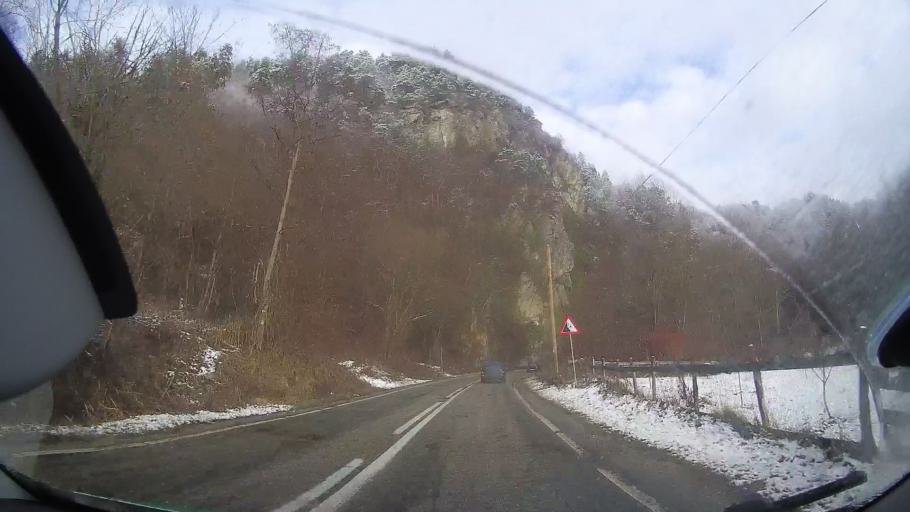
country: RO
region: Alba
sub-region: Oras Baia de Aries
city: Baia de Aries
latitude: 46.4004
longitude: 23.3014
